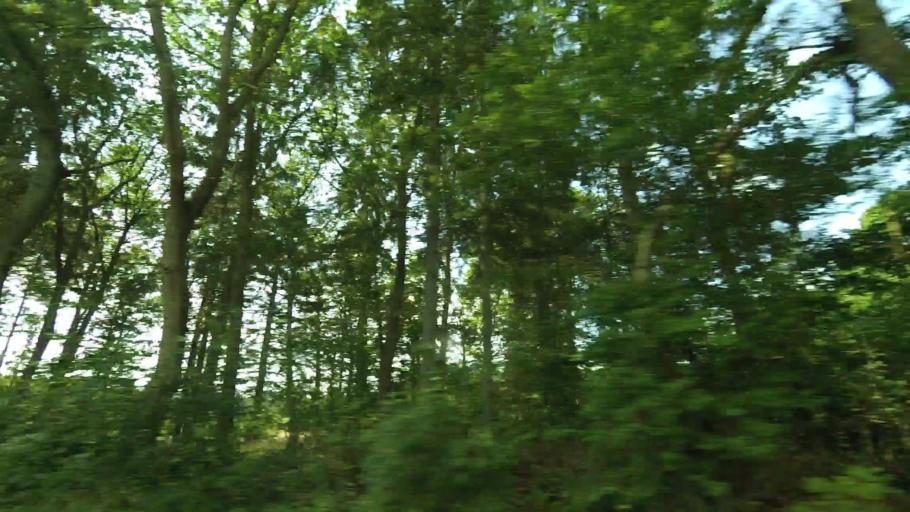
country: DK
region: Central Jutland
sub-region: Syddjurs Kommune
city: Ryomgard
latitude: 56.4624
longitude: 10.5265
